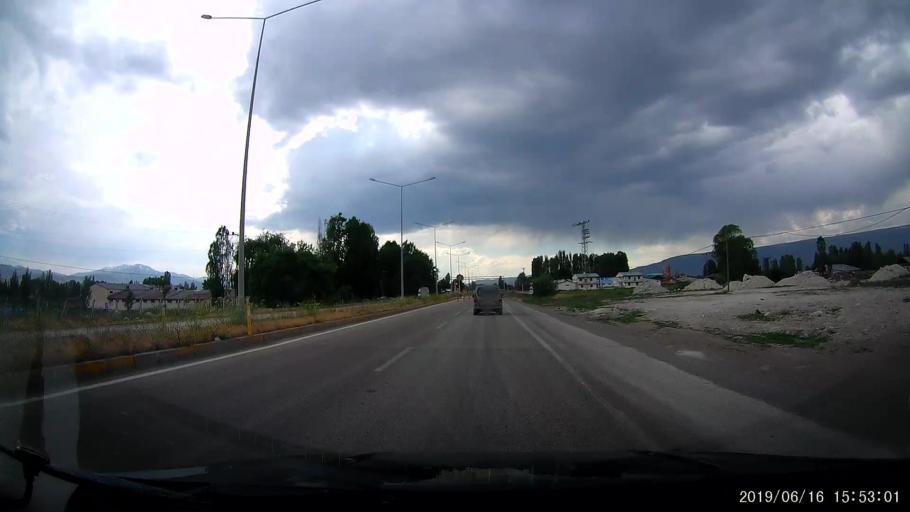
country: TR
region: Erzurum
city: Pasinler
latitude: 39.9774
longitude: 41.6525
